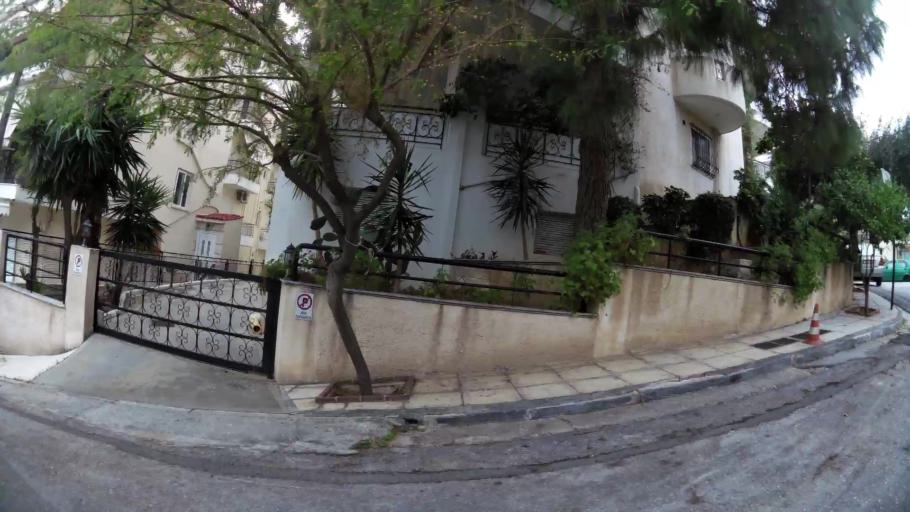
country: GR
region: Attica
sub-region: Nomarchia Athinas
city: Alimos
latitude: 37.9189
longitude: 23.7322
